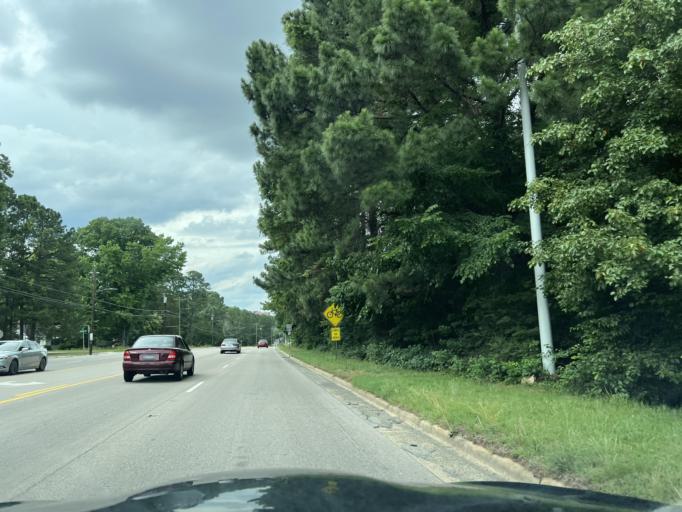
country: US
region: North Carolina
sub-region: Durham County
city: Durham
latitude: 35.9621
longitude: -78.8941
